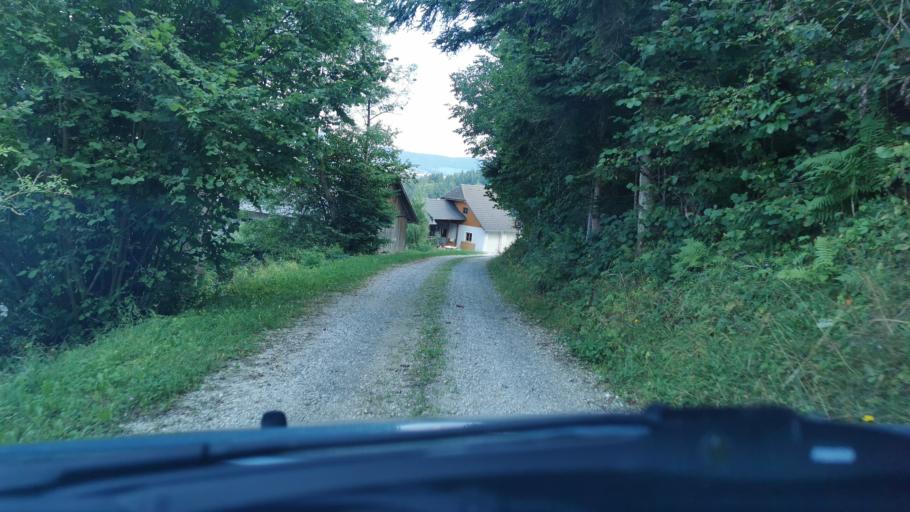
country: AT
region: Styria
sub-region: Politischer Bezirk Weiz
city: Koglhof
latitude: 47.3121
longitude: 15.6697
